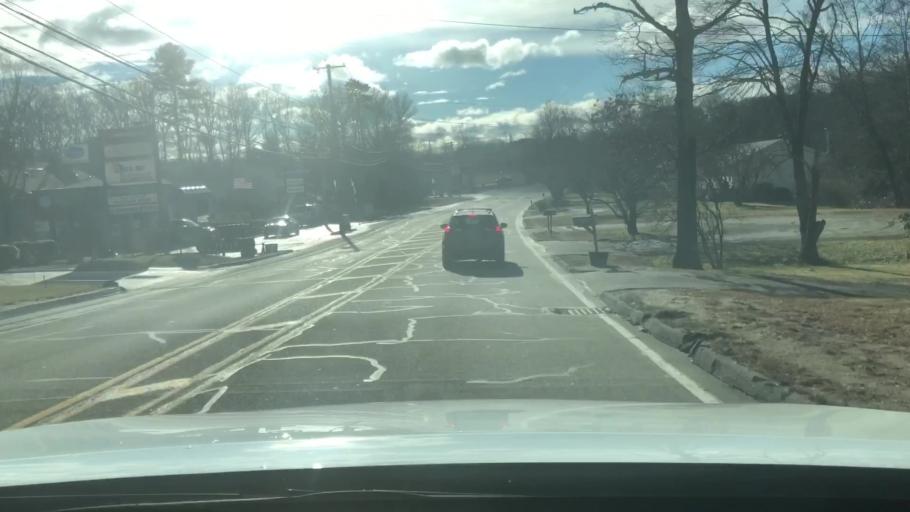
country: US
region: Massachusetts
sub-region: Norfolk County
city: Bellingham
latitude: 42.0541
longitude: -71.4846
